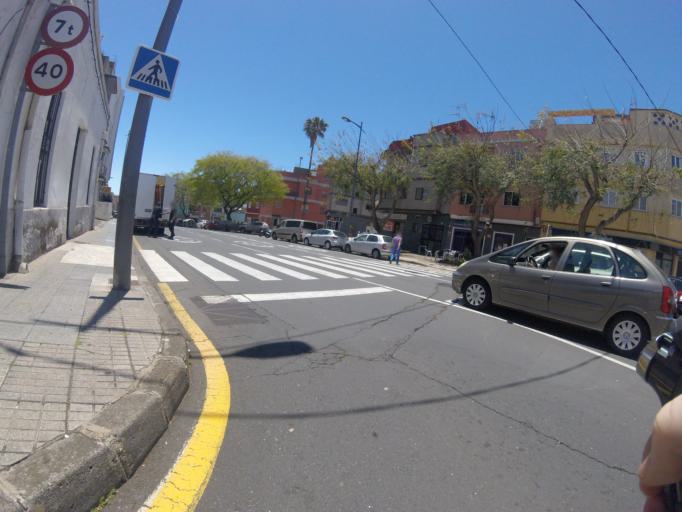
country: ES
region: Canary Islands
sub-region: Provincia de Santa Cruz de Tenerife
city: La Laguna
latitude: 28.4887
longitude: -16.3224
